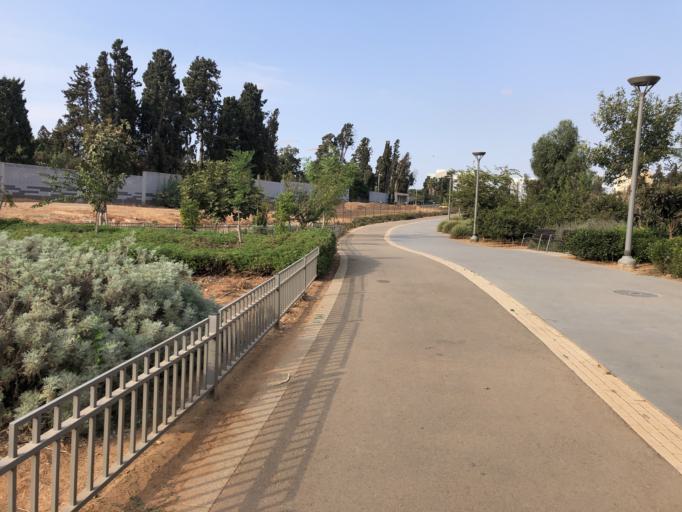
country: IL
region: Tel Aviv
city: Giv`at Shemu'el
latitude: 32.0578
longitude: 34.8452
